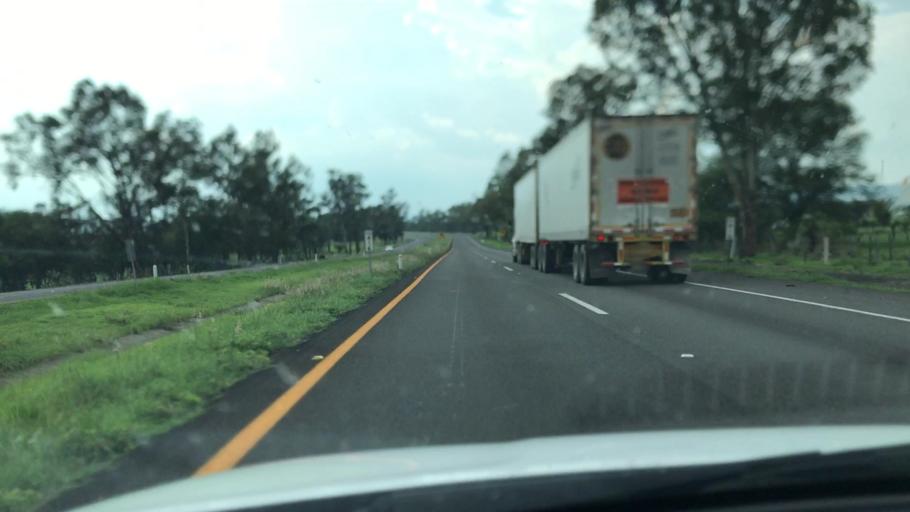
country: MX
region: Jalisco
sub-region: Ocotlan
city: Joconoxtle (La Tuna)
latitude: 20.3688
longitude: -102.6542
